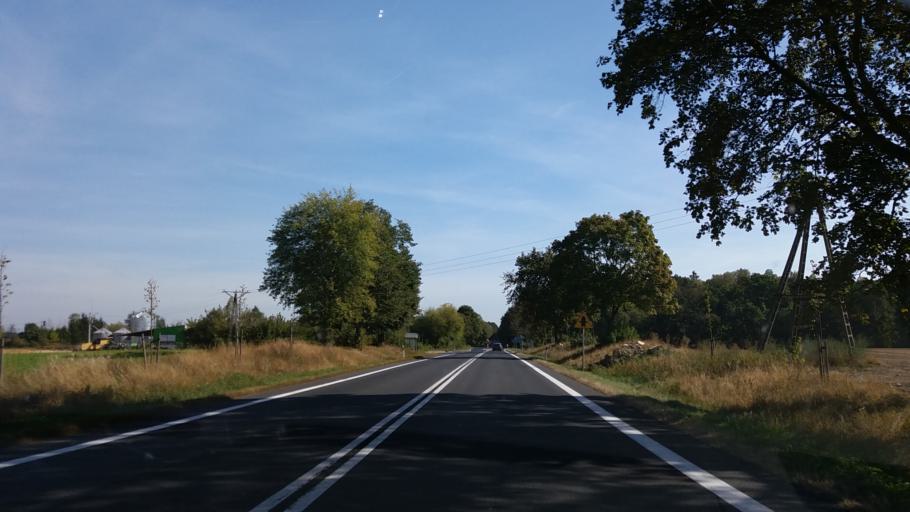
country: PL
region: Greater Poland Voivodeship
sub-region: Powiat miedzychodzki
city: Kwilcz
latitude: 52.5444
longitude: 16.1230
